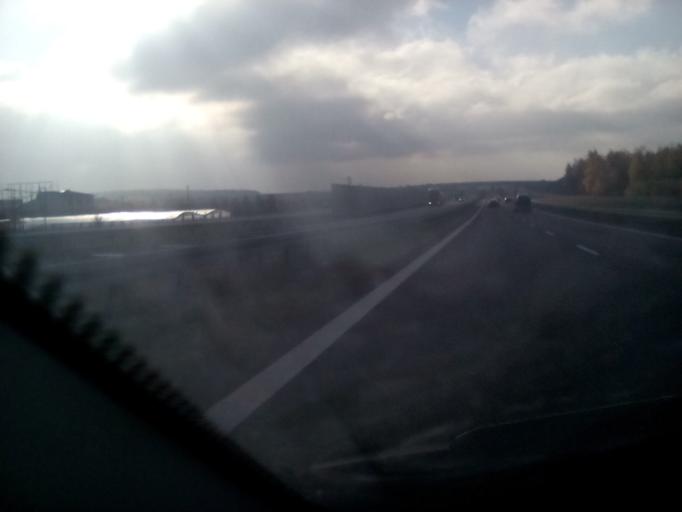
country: PL
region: Masovian Voivodeship
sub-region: Powiat bialobrzeski
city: Promna
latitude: 51.7138
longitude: 20.9239
